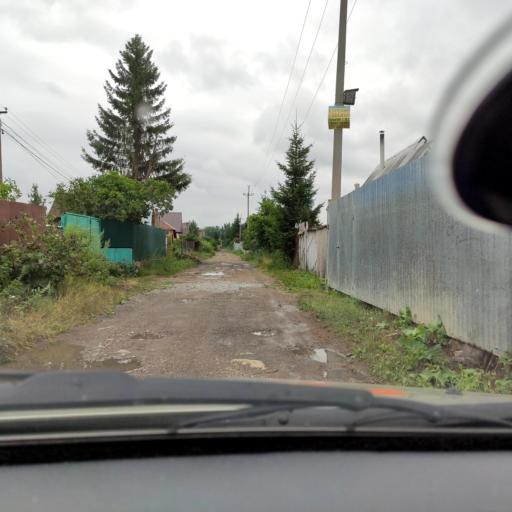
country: RU
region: Bashkortostan
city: Iglino
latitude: 54.7875
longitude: 56.1912
